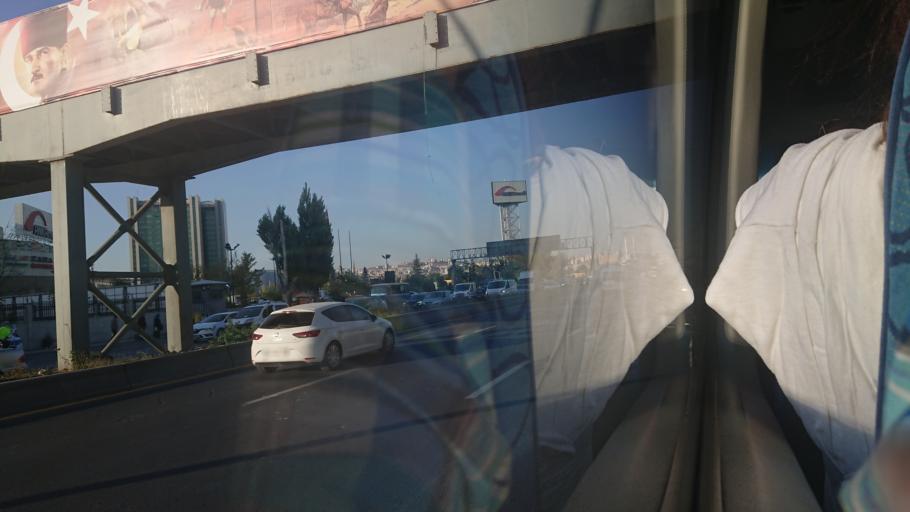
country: TR
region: Ankara
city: Ankara
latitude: 39.9483
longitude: 32.8331
